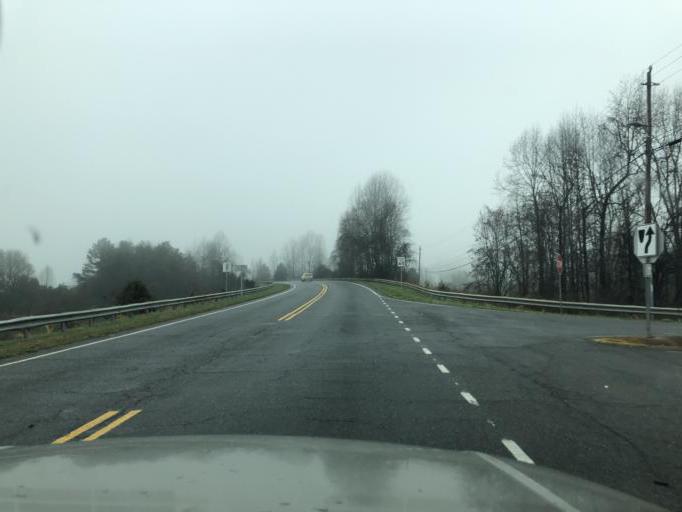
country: US
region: North Carolina
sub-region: Gaston County
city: Cherryville
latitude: 35.3590
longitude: -81.4352
